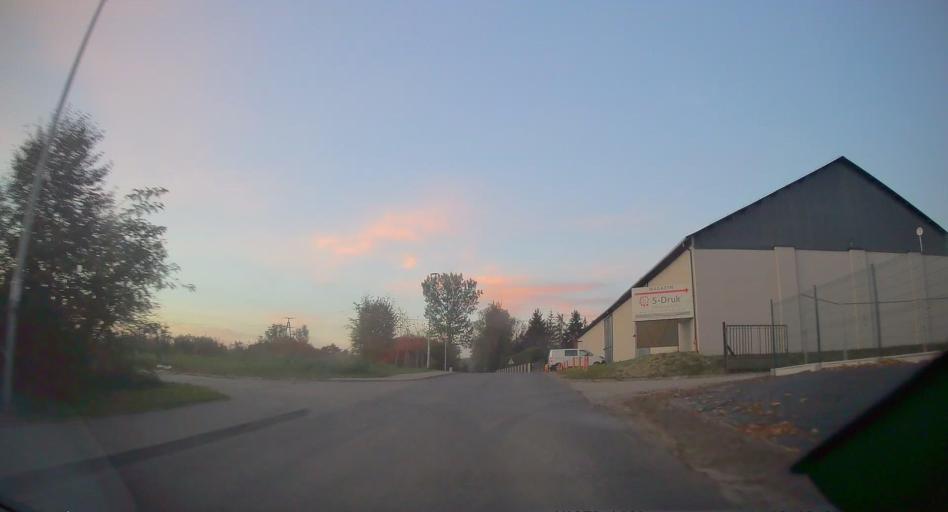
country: PL
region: Lesser Poland Voivodeship
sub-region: Powiat krakowski
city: Zabierzow
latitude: 50.1273
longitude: 19.8219
